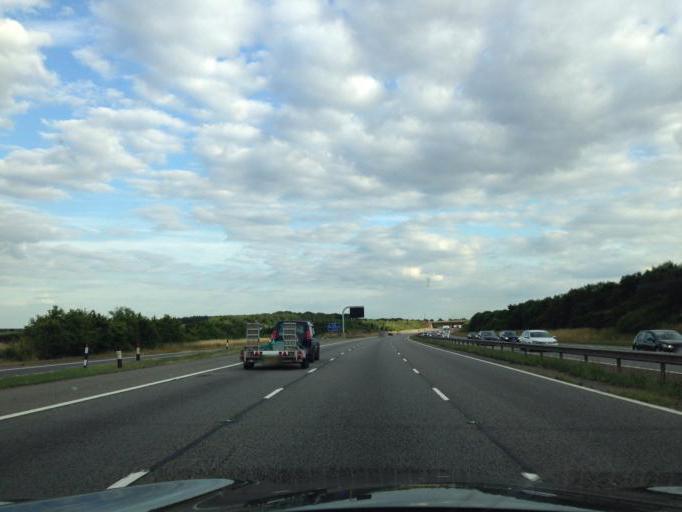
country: GB
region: England
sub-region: Oxfordshire
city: Somerton
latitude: 51.9544
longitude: -1.2100
